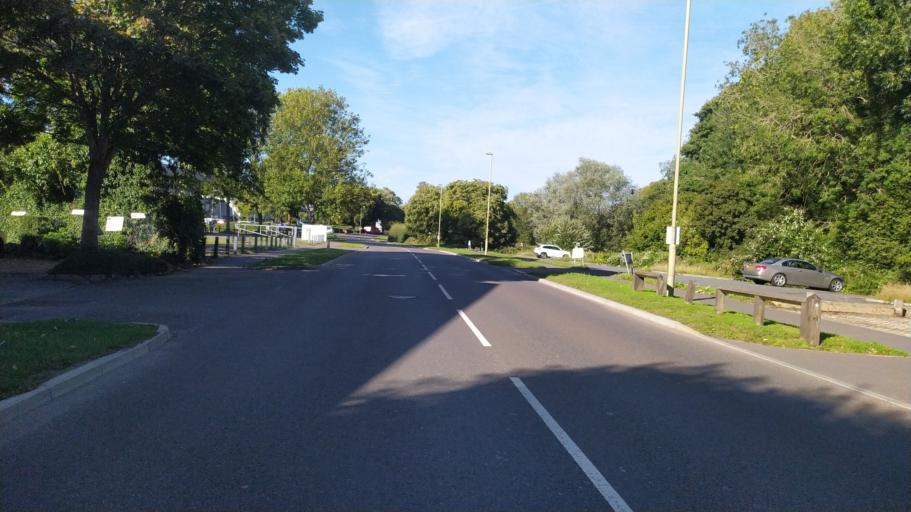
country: GB
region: England
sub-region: Hampshire
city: Alton
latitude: 51.1555
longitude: -0.9571
